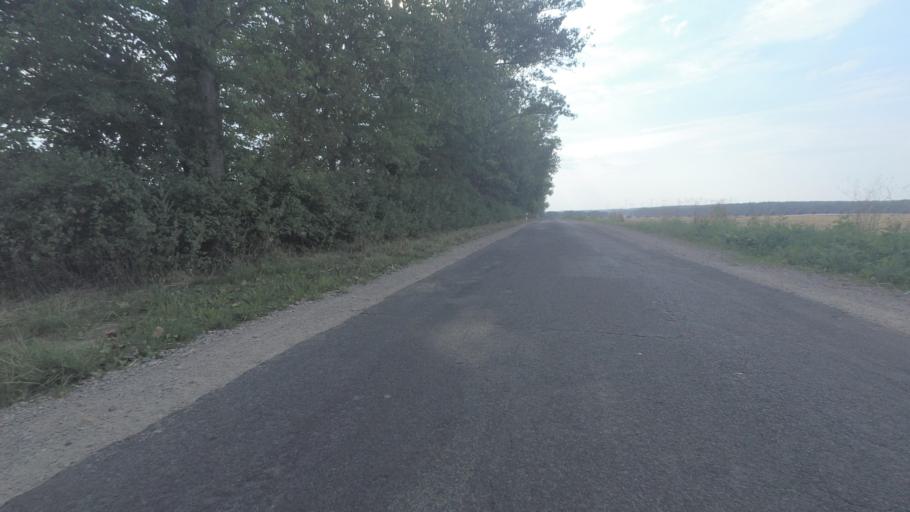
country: DE
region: Brandenburg
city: Heiligengrabe
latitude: 53.2437
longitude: 12.3981
